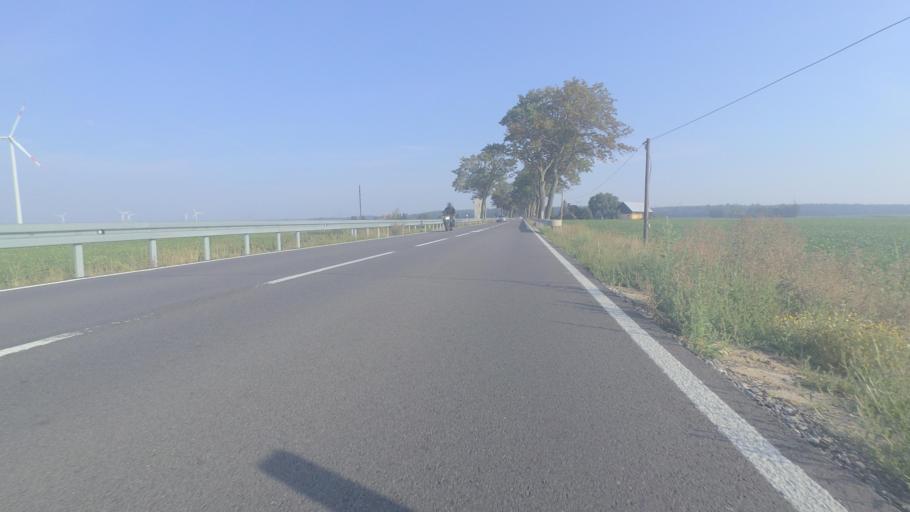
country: DE
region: Mecklenburg-Vorpommern
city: Gormin
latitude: 54.0125
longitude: 13.1406
